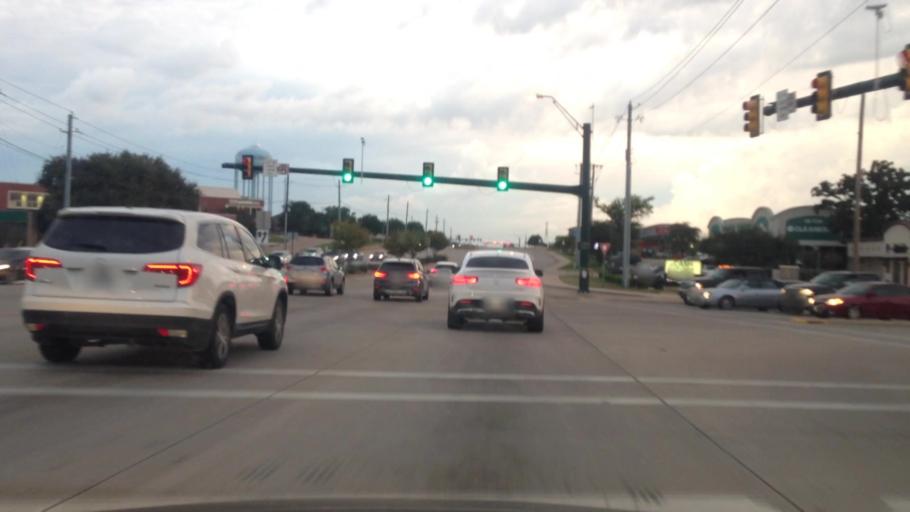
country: US
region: Texas
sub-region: Tarrant County
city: Hurst
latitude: 32.8448
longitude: -97.1860
